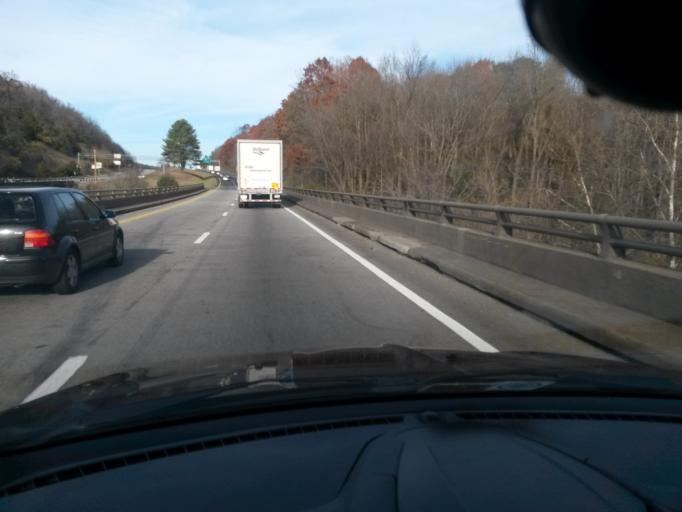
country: US
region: Virginia
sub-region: Botetourt County
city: Cloverdale
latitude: 37.3781
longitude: -79.9094
